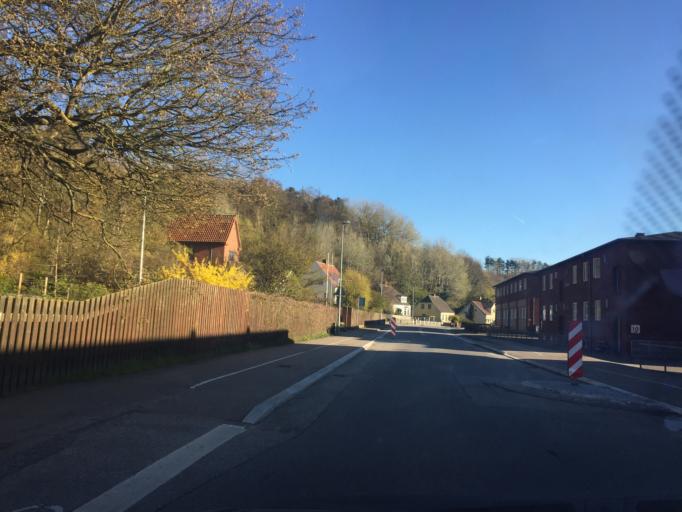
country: DK
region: Capital Region
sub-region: Halsnaes Kommune
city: Frederiksvaerk
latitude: 55.9634
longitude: 12.0215
